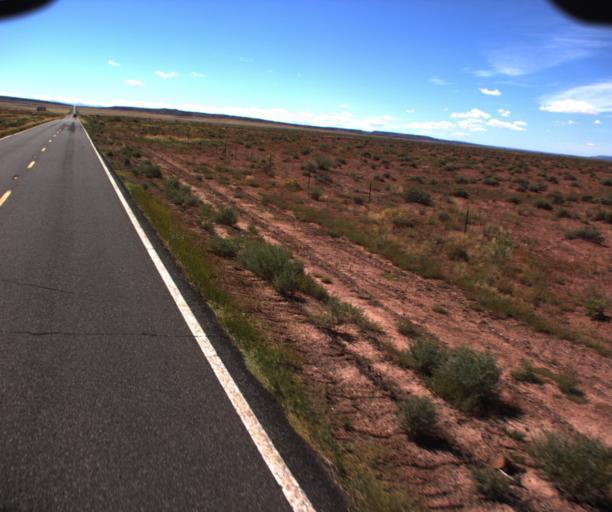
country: US
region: Arizona
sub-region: Apache County
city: Saint Johns
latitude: 34.7009
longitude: -109.2710
